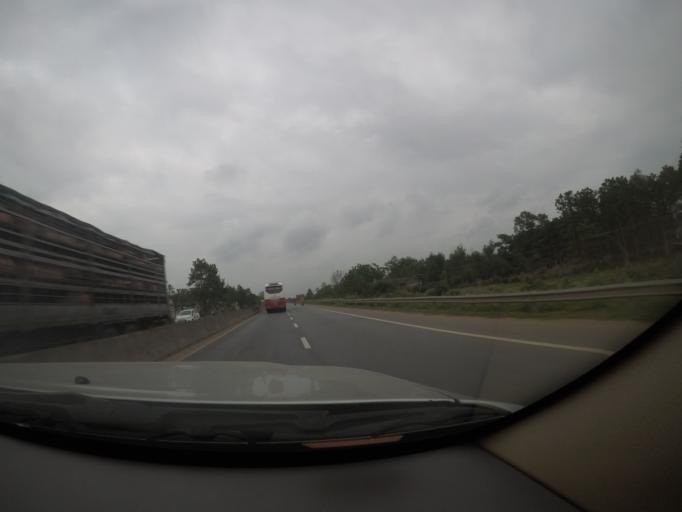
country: VN
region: Quang Tri
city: Hai Lang
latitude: 16.6574
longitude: 107.2801
